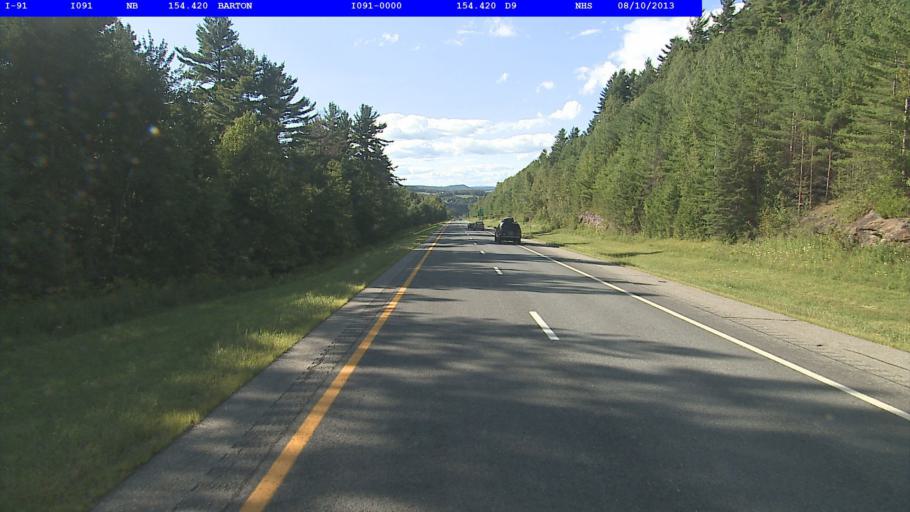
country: US
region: Vermont
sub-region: Orleans County
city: Newport
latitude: 44.7152
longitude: -72.1737
